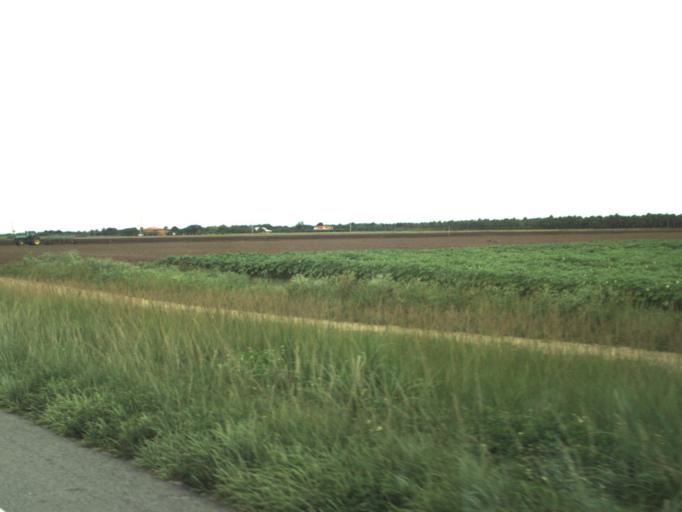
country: US
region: Florida
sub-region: Miami-Dade County
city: The Hammocks
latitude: 25.6455
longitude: -80.4803
